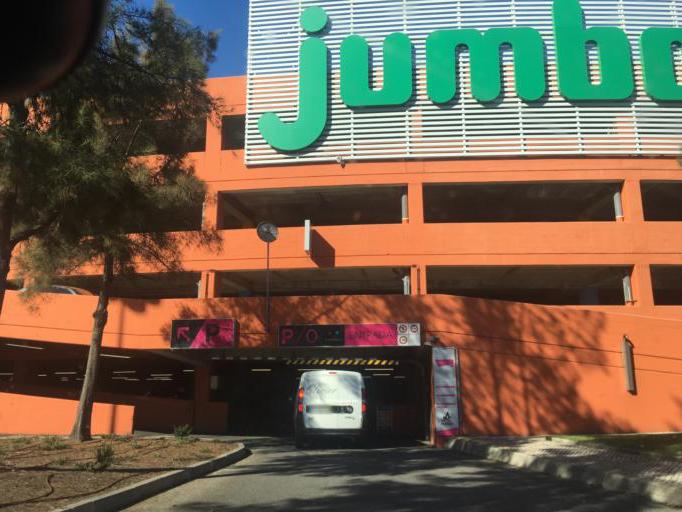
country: PT
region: Lisbon
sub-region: Oeiras
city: Alges
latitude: 38.7266
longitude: -9.2180
